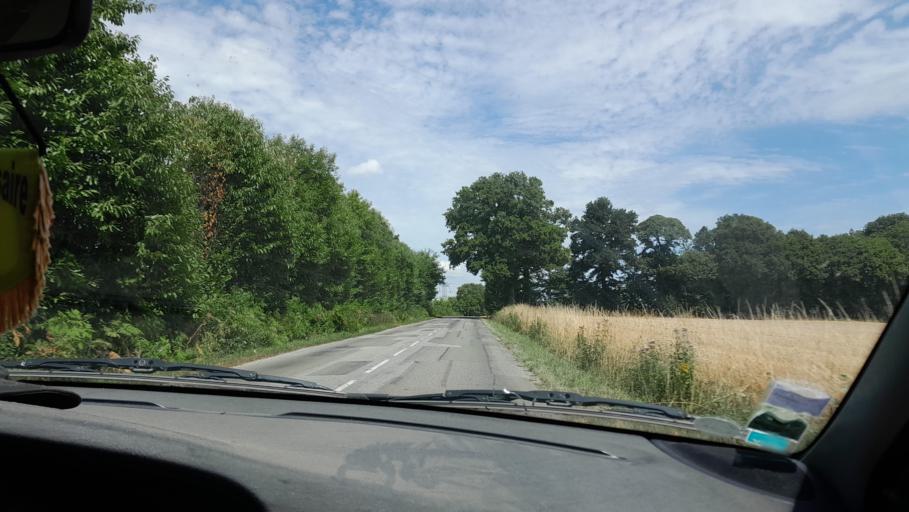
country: FR
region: Brittany
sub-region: Departement d'Ille-et-Vilaine
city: Le Pertre
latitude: 48.0557
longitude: -1.0324
